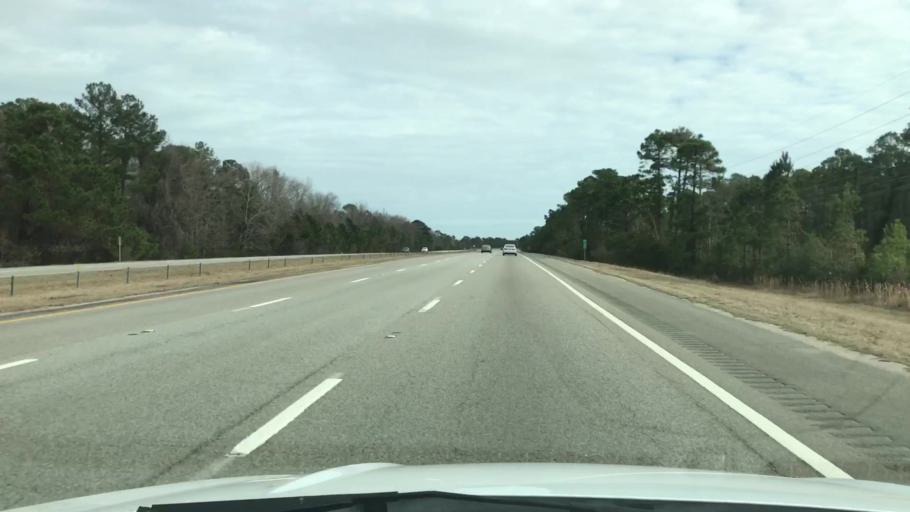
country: US
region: South Carolina
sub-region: Horry County
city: Forestbrook
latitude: 33.7482
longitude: -78.9073
